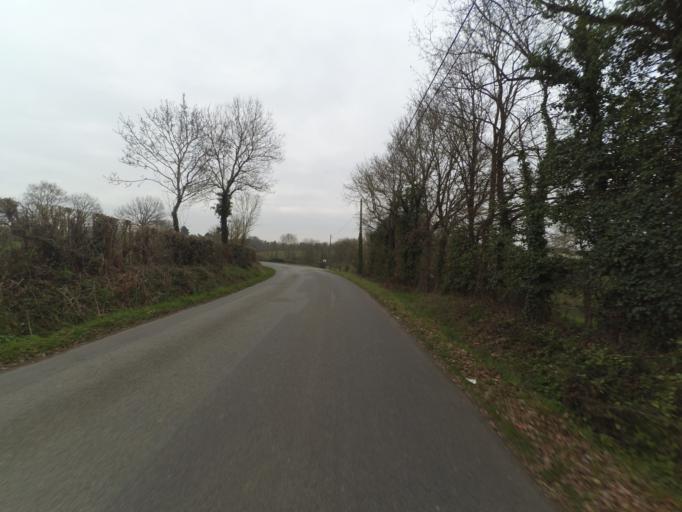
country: FR
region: Pays de la Loire
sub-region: Departement de la Loire-Atlantique
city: Coueron
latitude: 47.2348
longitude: -1.6969
